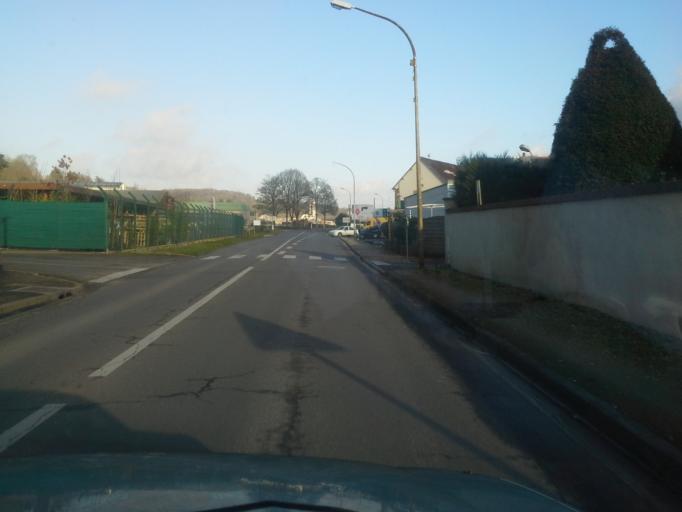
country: FR
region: Centre
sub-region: Departement du Loir-et-Cher
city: Naveil
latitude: 47.7994
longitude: 1.0274
